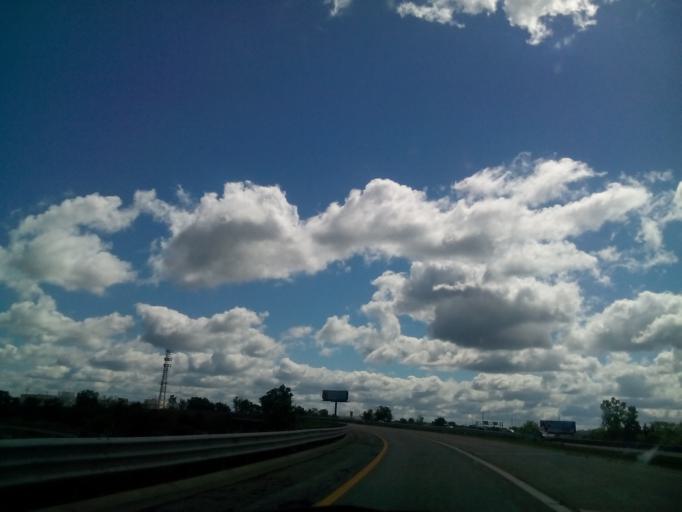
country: US
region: Michigan
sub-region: Genesee County
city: Flint
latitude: 42.9831
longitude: -83.7341
